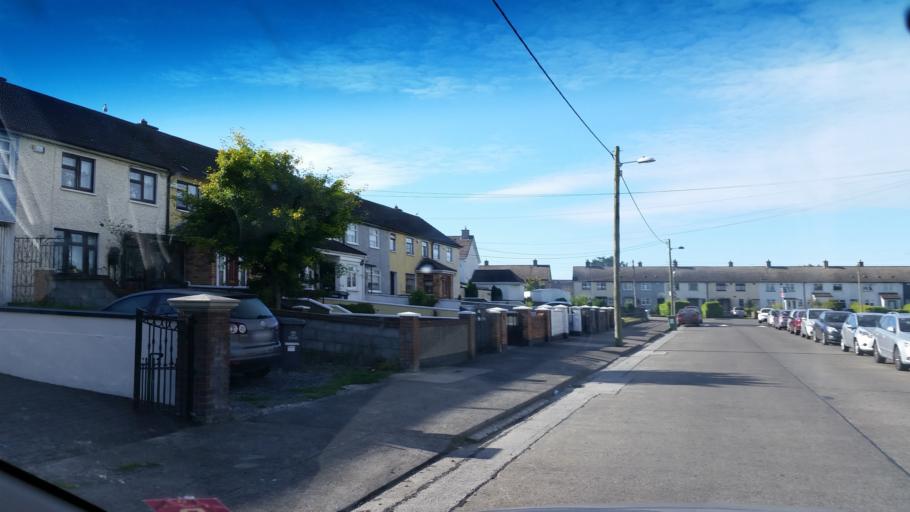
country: IE
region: Leinster
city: Artane
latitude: 53.3942
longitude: -6.2261
